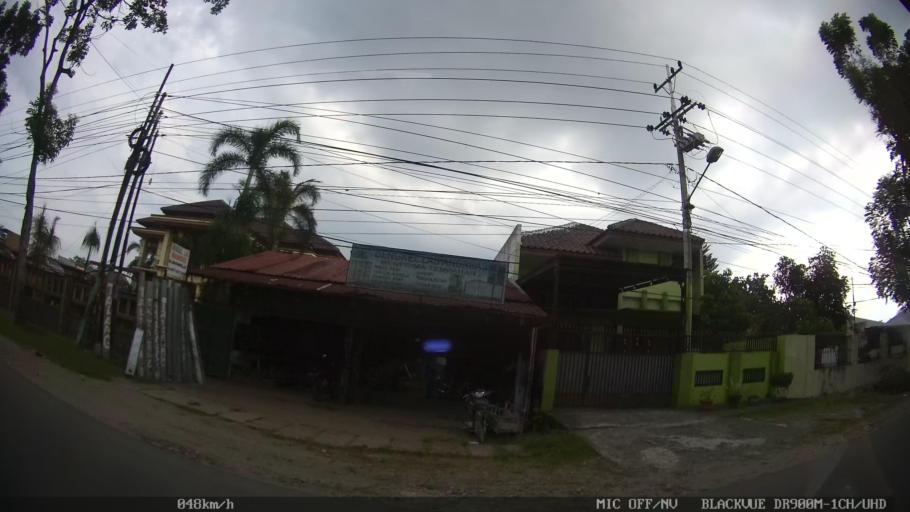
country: ID
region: North Sumatra
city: Sunggal
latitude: 3.5408
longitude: 98.6280
